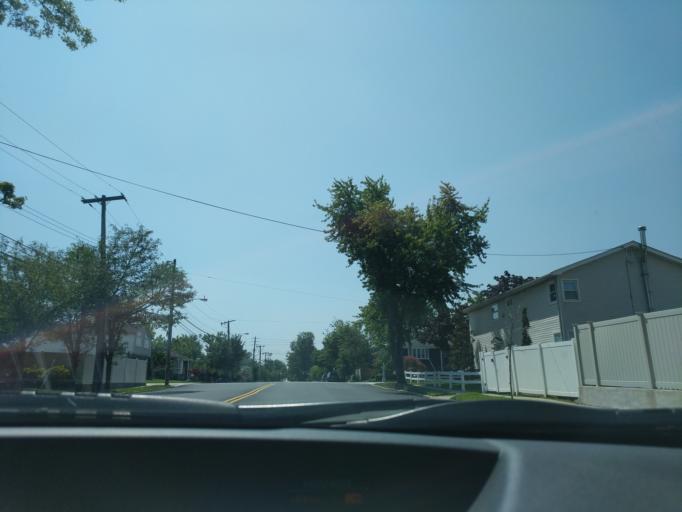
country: US
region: New Jersey
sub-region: Middlesex County
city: Carteret
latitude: 40.5410
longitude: -74.1964
